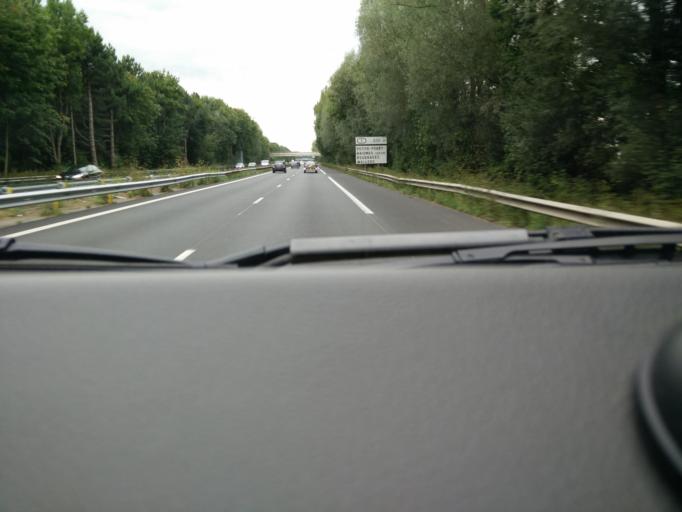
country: FR
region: Nord-Pas-de-Calais
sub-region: Departement du Nord
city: Petite-Foret
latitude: 50.3721
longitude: 3.4788
